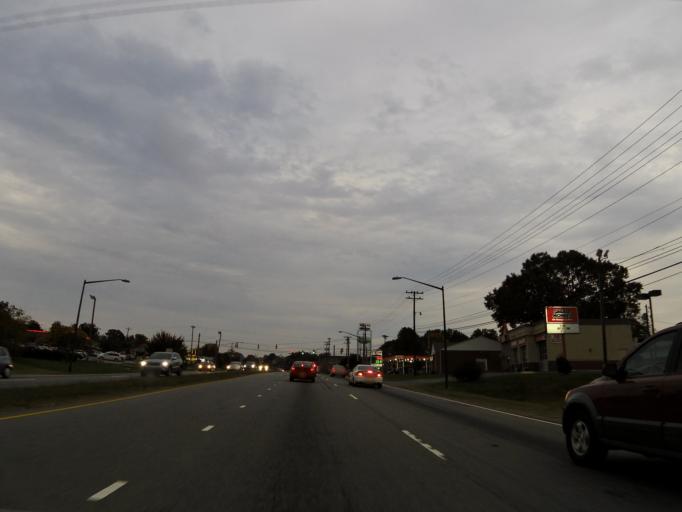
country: US
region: North Carolina
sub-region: Catawba County
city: Longview
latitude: 35.7365
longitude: -81.3658
